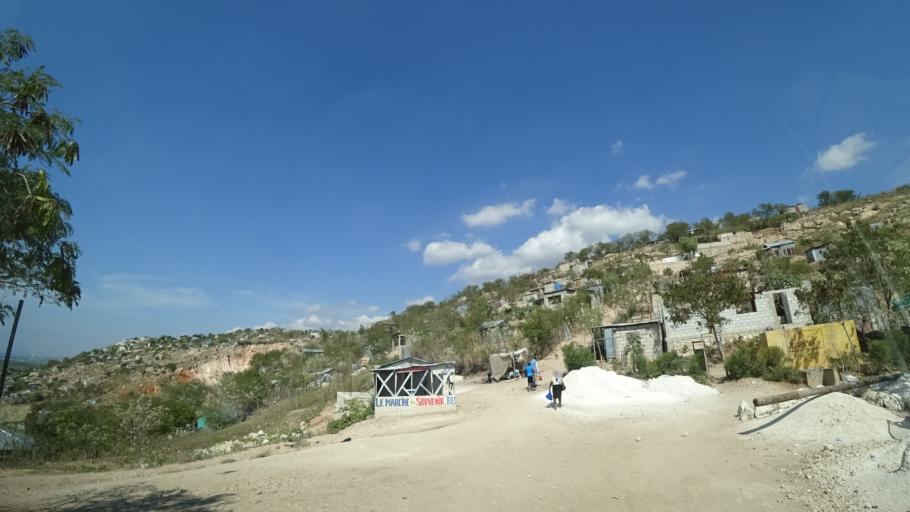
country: HT
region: Ouest
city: Croix des Bouquets
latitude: 18.6616
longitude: -72.2868
